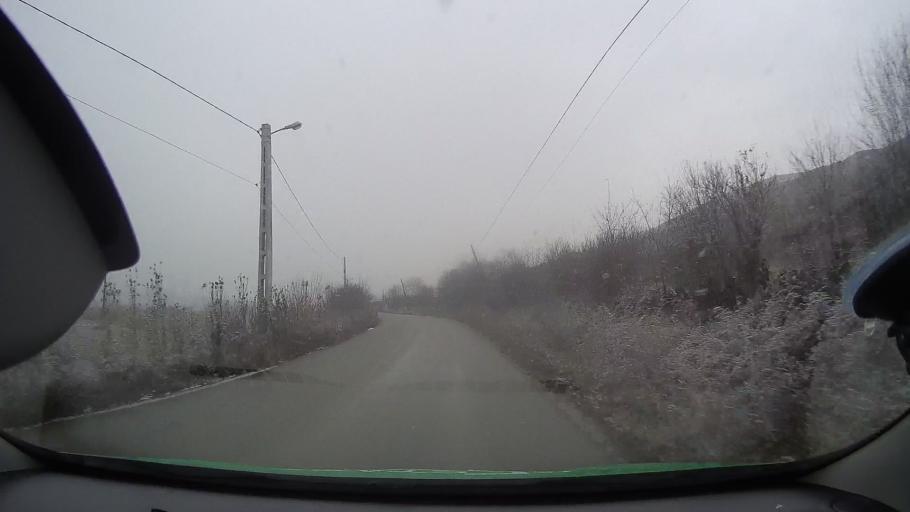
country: RO
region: Alba
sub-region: Comuna Farau
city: Farau
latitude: 46.3382
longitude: 23.9533
